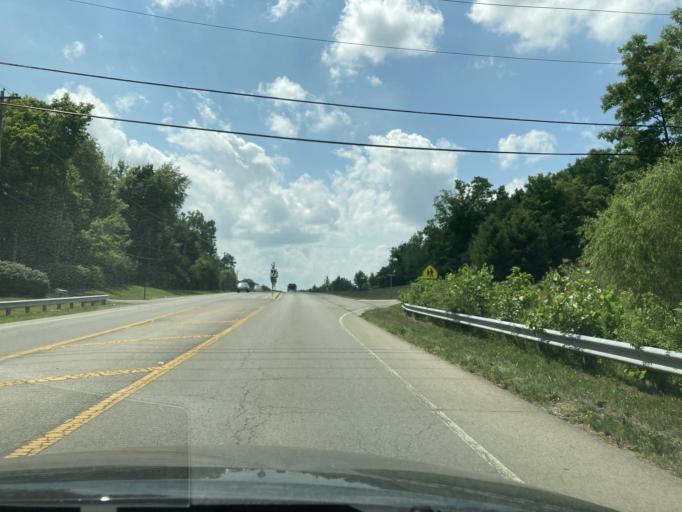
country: US
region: Indiana
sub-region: Boone County
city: Zionsville
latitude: 39.9988
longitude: -86.2443
